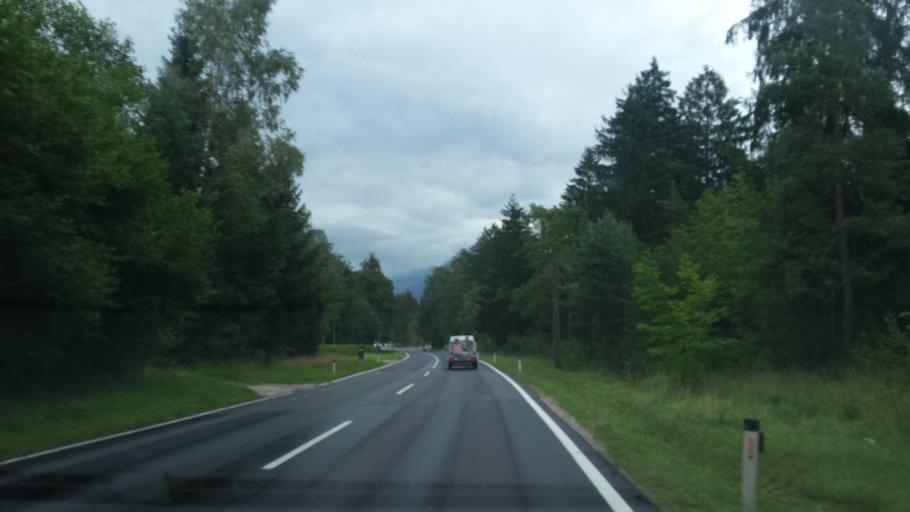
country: AT
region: Upper Austria
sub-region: Politischer Bezirk Gmunden
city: Bad Ischl
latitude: 47.7158
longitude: 13.5699
